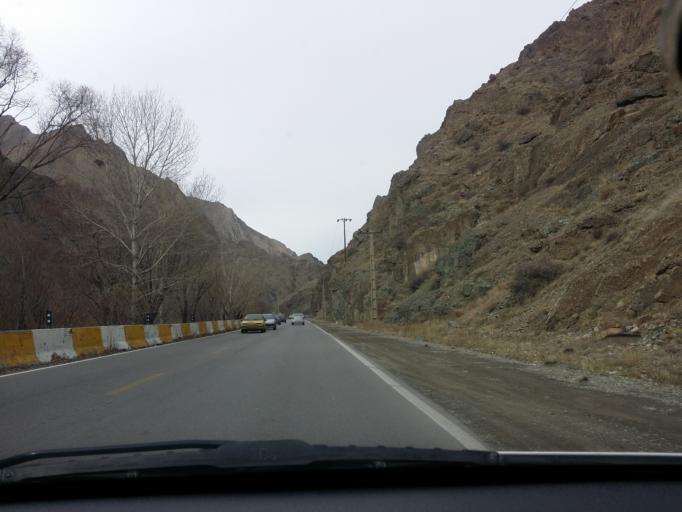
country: IR
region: Tehran
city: Tajrish
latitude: 36.0141
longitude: 51.2886
